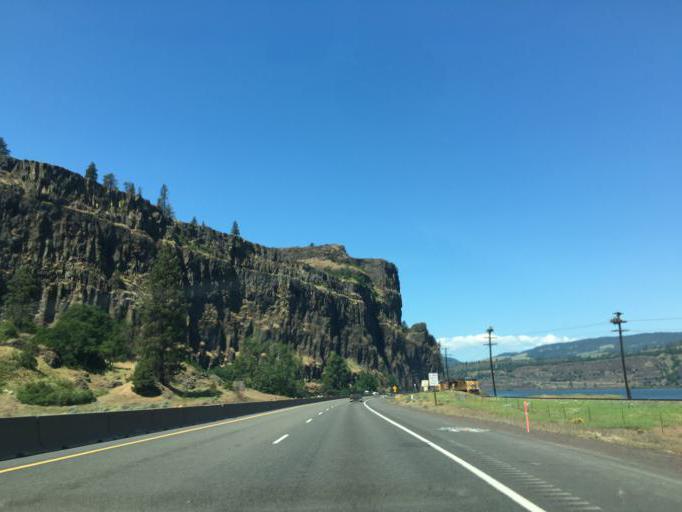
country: US
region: Oregon
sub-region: Wasco County
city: Chenoweth
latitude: 45.6851
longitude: -121.2951
